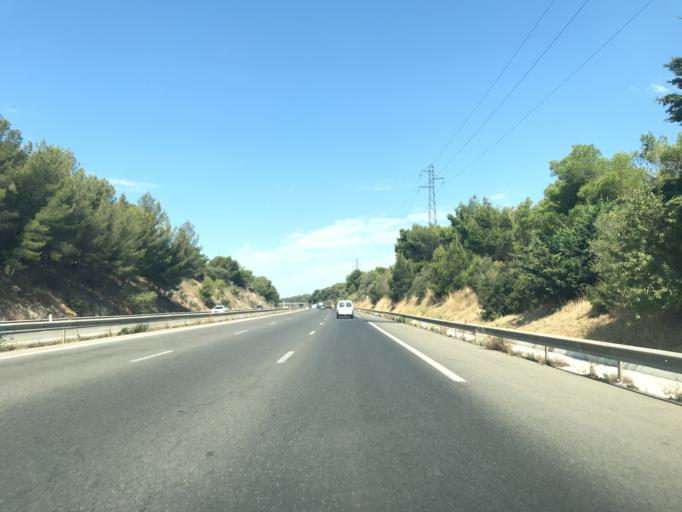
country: FR
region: Provence-Alpes-Cote d'Azur
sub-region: Departement du Var
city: Sanary-sur-Mer
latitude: 43.1363
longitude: 5.8069
